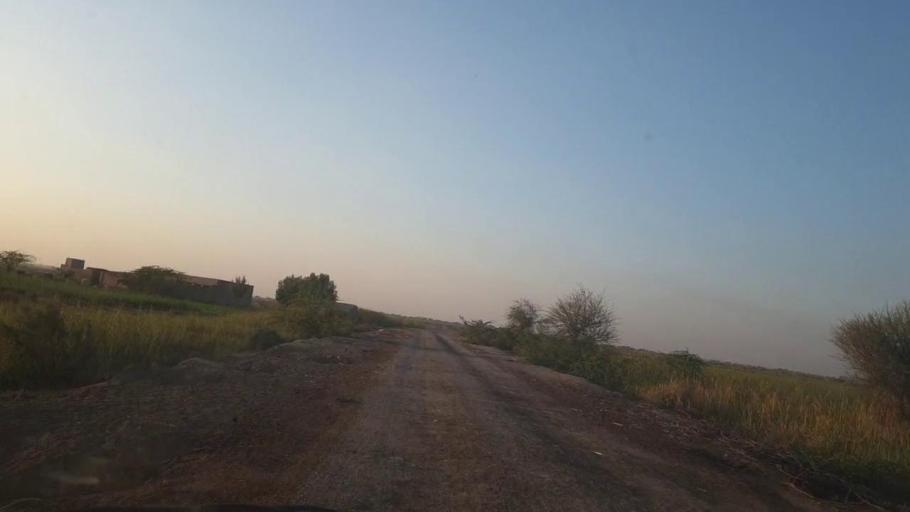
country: PK
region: Sindh
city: Mirpur Khas
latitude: 25.4539
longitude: 69.0745
